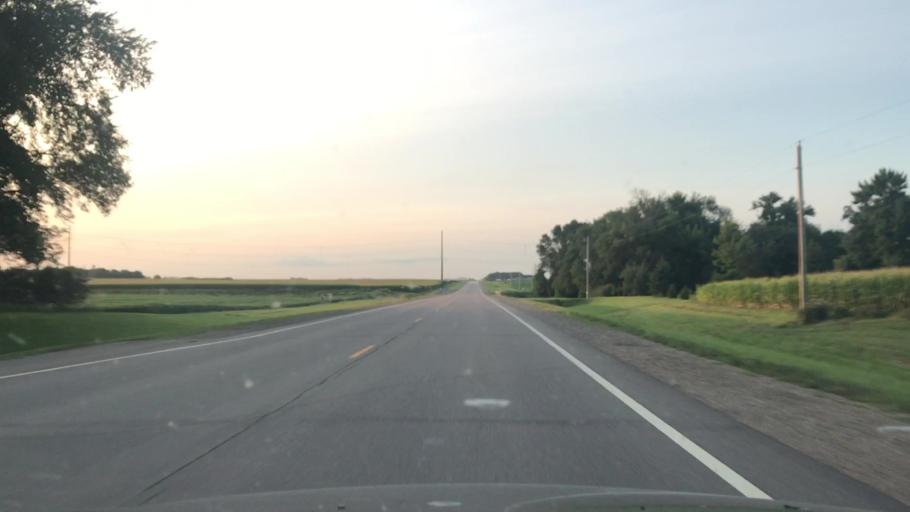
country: US
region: Minnesota
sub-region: Redwood County
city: Redwood Falls
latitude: 44.4281
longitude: -95.1176
